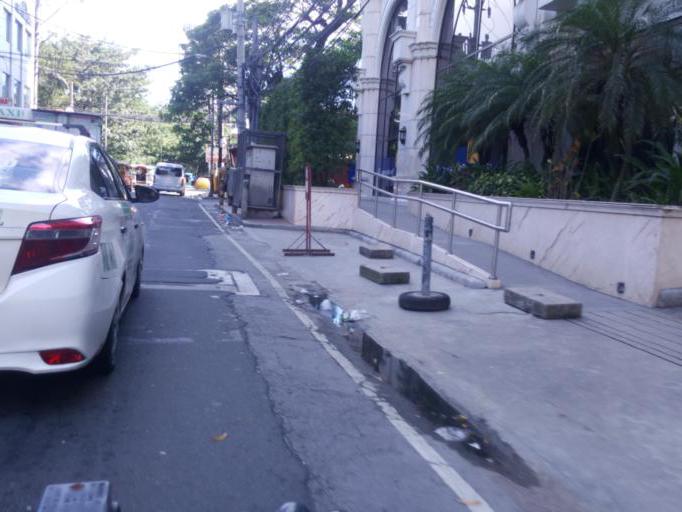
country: PH
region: Metro Manila
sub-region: City of Manila
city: Port Area
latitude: 14.5659
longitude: 120.9859
